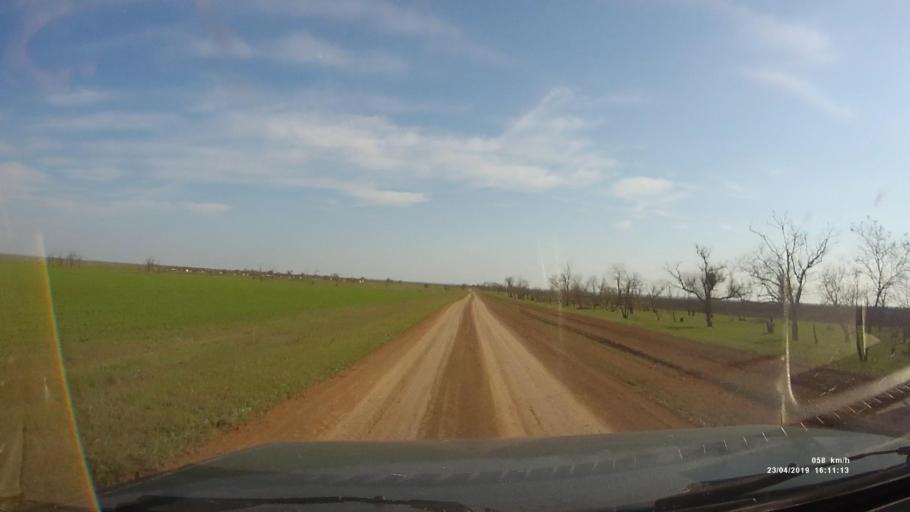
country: RU
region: Rostov
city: Remontnoye
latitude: 46.4758
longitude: 43.1231
